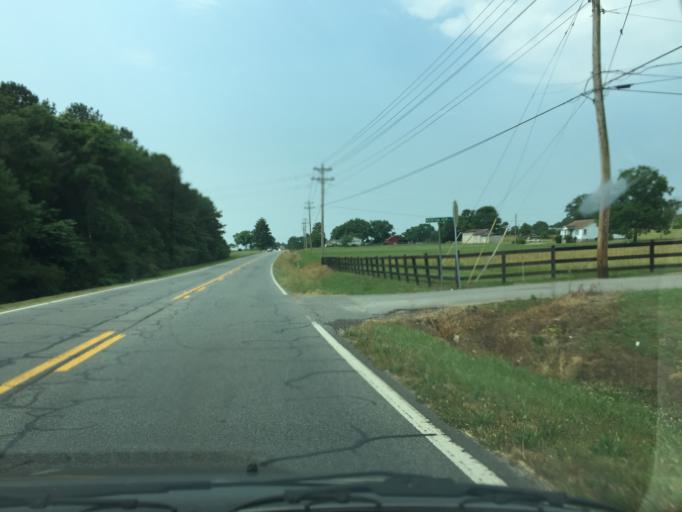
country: US
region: Georgia
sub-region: Catoosa County
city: Ringgold
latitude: 34.8784
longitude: -85.1394
